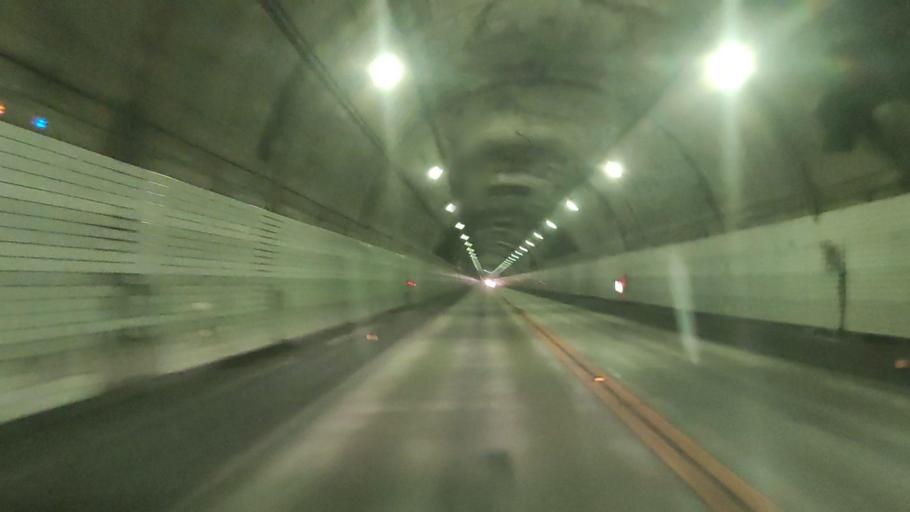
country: JP
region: Fukuoka
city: Maebaru-chuo
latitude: 33.4726
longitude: 130.2841
